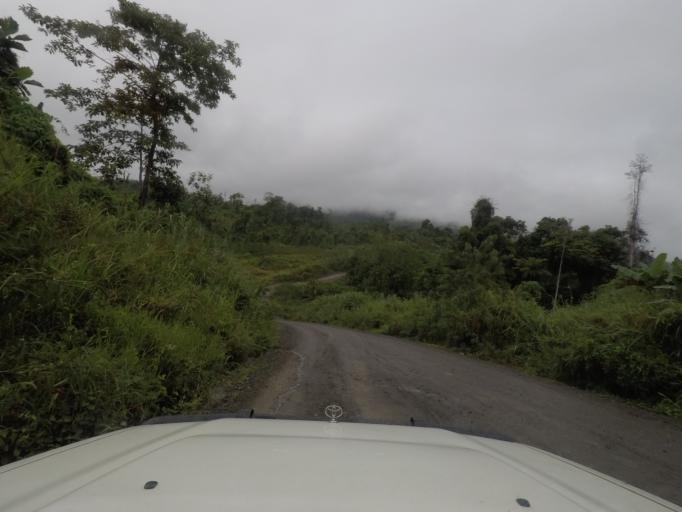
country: PG
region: Madang
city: Madang
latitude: -5.4855
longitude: 145.4841
